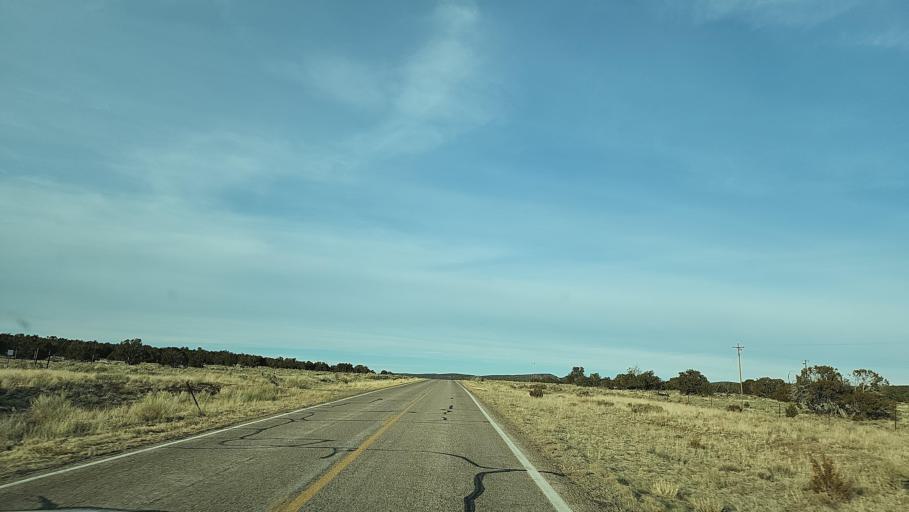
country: US
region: New Mexico
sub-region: McKinley County
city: Black Rock
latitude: 34.4106
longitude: -108.4348
